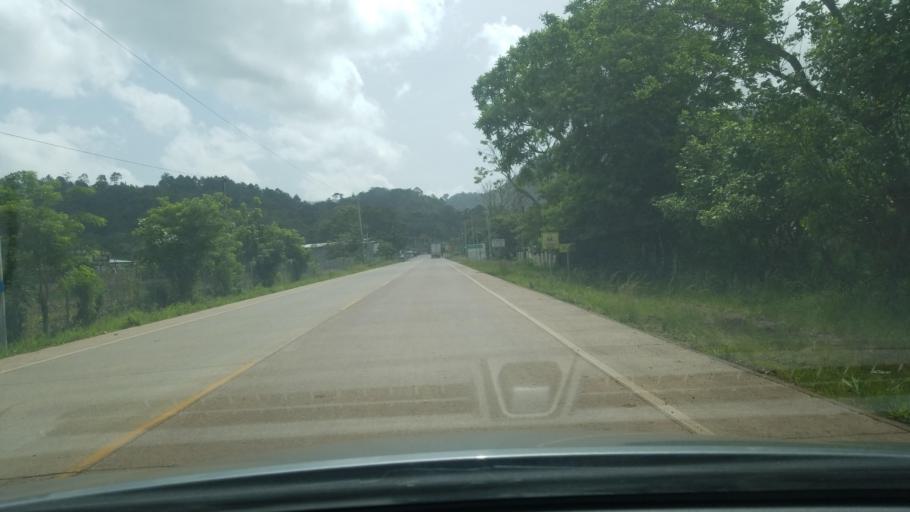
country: HN
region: Copan
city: San Agustin
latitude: 14.9167
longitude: -88.9888
